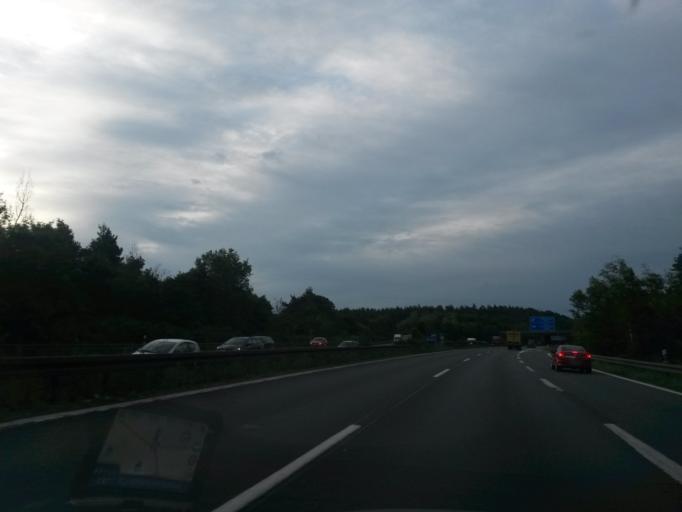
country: DE
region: Bavaria
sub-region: Regierungsbezirk Mittelfranken
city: Wendelstein
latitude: 49.3936
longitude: 11.1128
